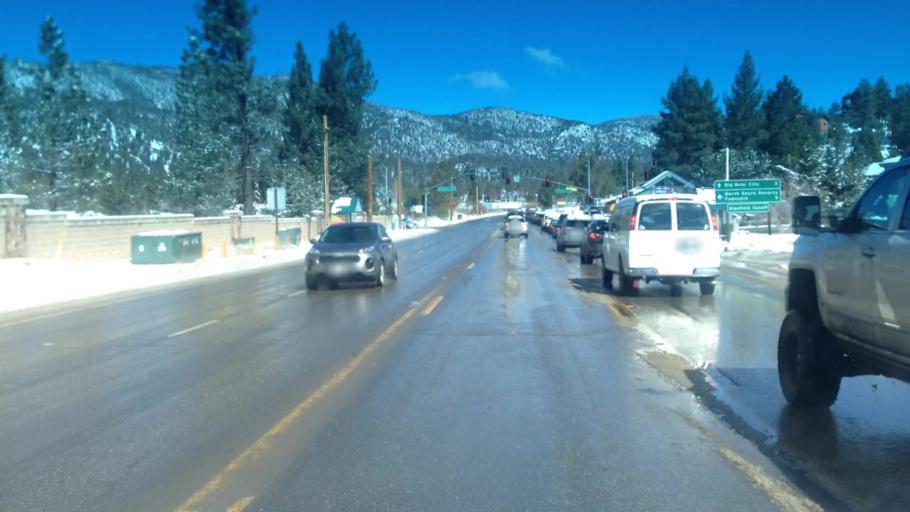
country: US
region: California
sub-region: San Bernardino County
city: Big Bear Lake
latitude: 34.2558
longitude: -116.8839
